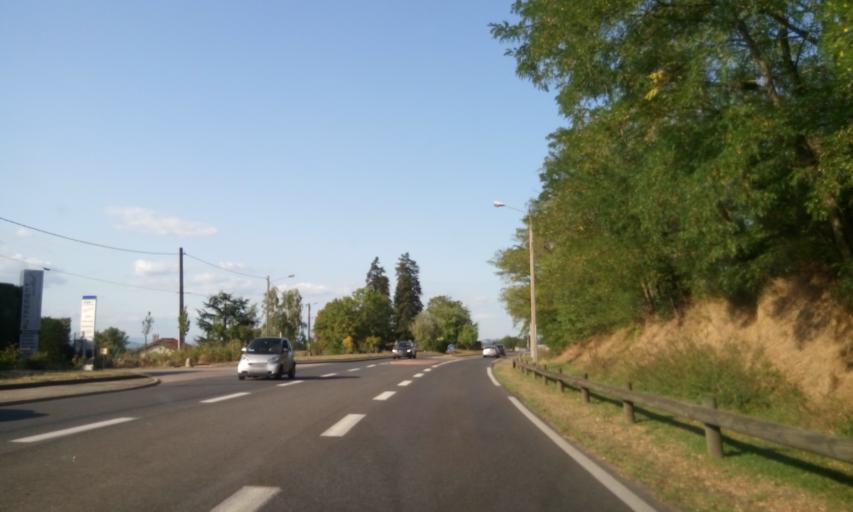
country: FR
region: Rhone-Alpes
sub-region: Departement du Rhone
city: Lissieu
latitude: 45.8672
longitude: 4.7425
